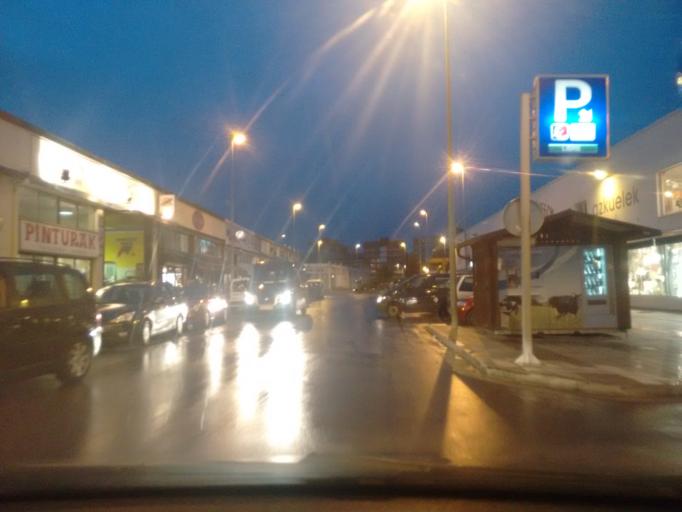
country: ES
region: Basque Country
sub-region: Provincia de Guipuzcoa
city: Zarautz
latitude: 43.2812
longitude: -2.1655
